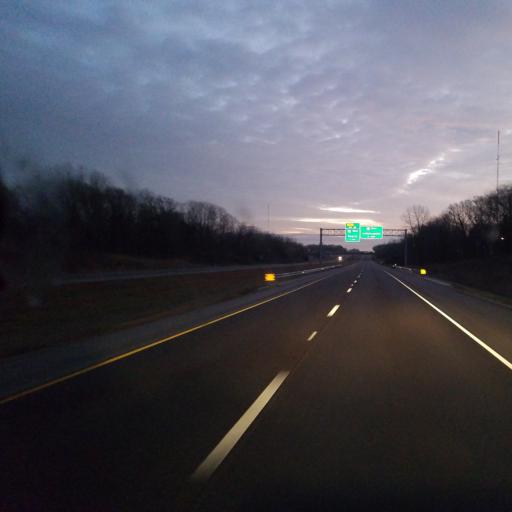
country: US
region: Illinois
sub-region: Tazewell County
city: Creve Coeur
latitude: 40.6304
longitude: -89.5575
